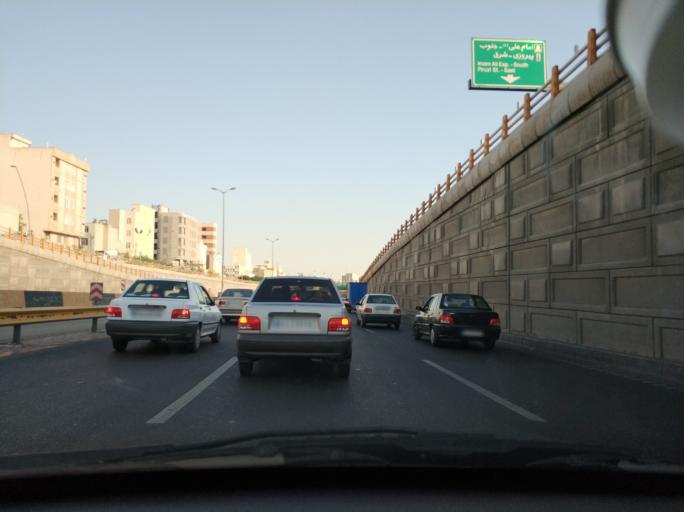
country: IR
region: Tehran
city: Tehran
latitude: 35.6928
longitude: 51.4567
